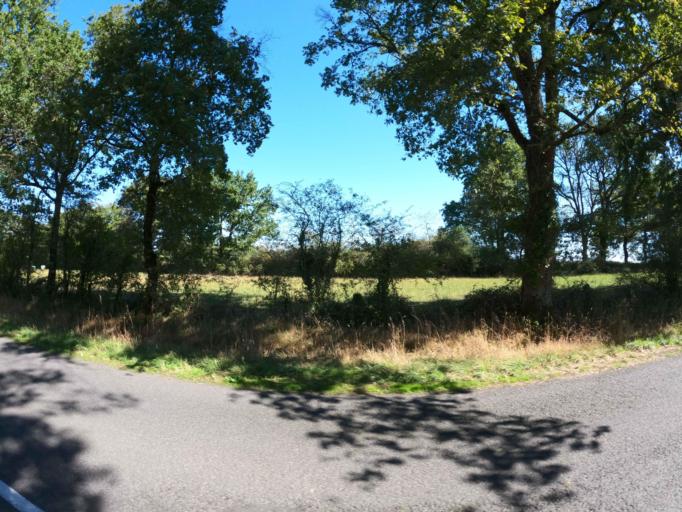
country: FR
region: Poitou-Charentes
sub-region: Departement de la Vienne
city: Lathus-Saint-Remy
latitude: 46.3239
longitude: 0.9692
